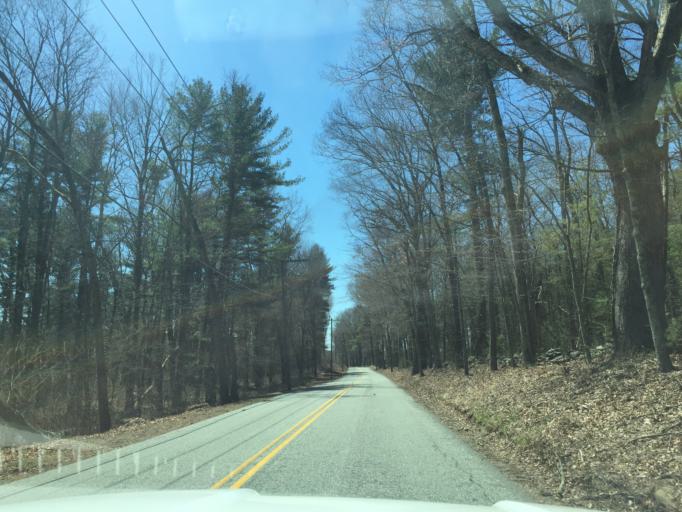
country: US
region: Connecticut
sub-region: Windham County
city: Quinebaug
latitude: 41.9991
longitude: -71.9511
